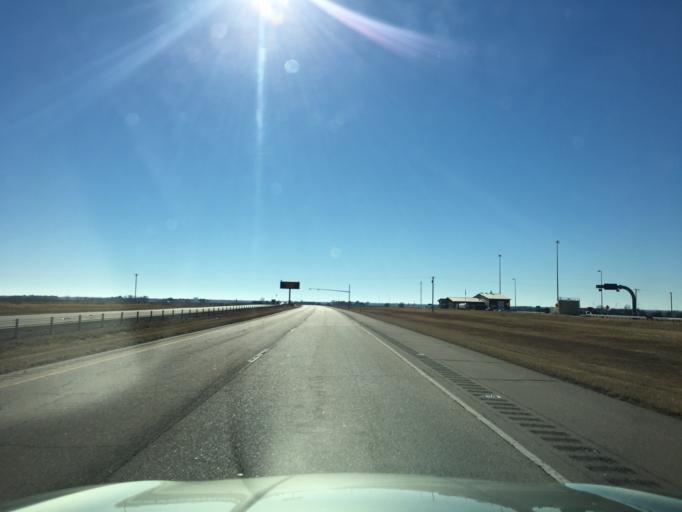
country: US
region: Oklahoma
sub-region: Kay County
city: Blackwell
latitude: 36.9870
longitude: -97.3455
